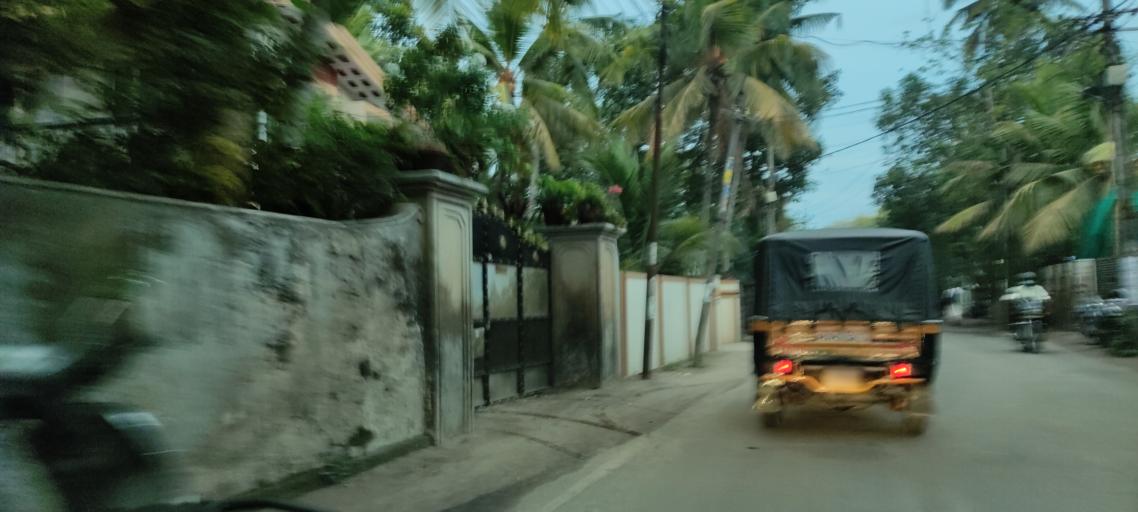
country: IN
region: Kerala
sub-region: Alappuzha
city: Shertallai
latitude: 9.6884
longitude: 76.3453
